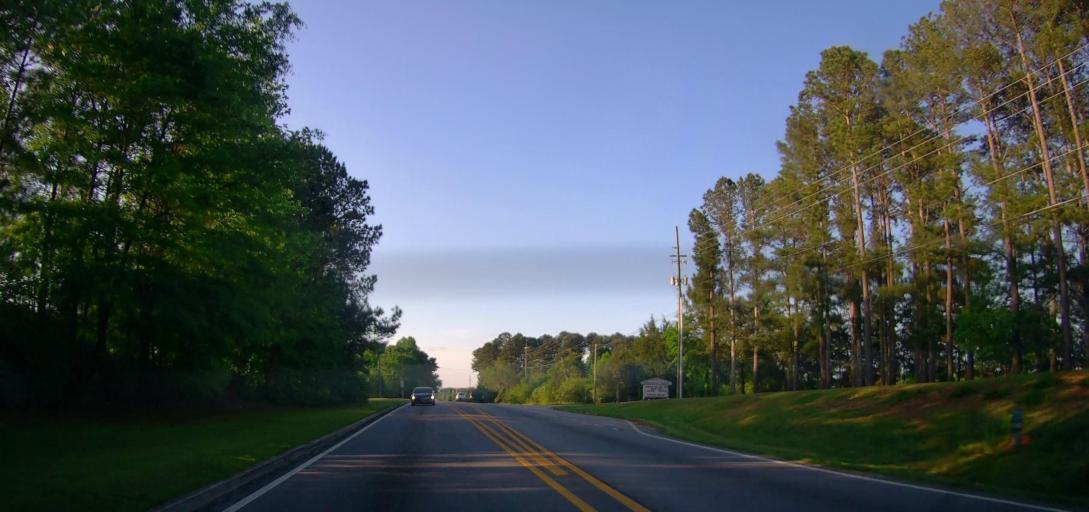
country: US
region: Georgia
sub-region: Newton County
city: Covington
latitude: 33.5849
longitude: -83.8343
